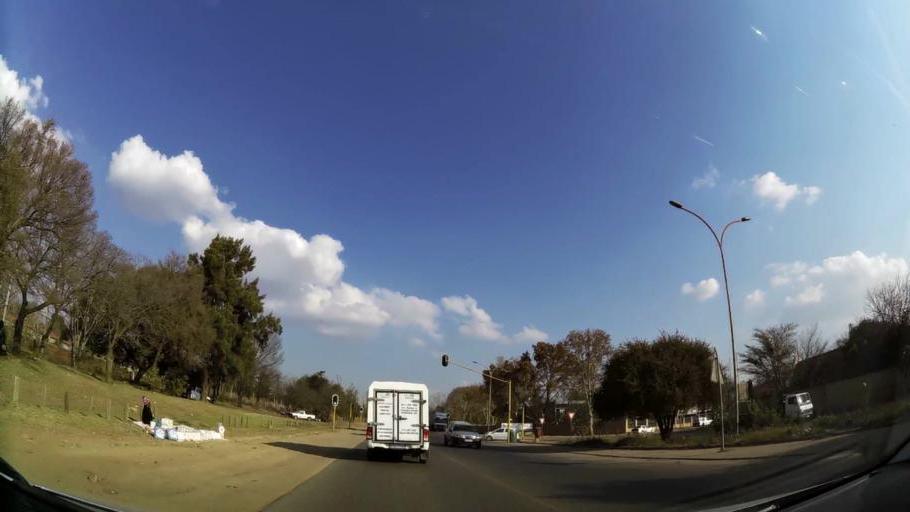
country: ZA
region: Gauteng
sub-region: Ekurhuleni Metropolitan Municipality
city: Tembisa
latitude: -25.9521
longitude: 28.2328
